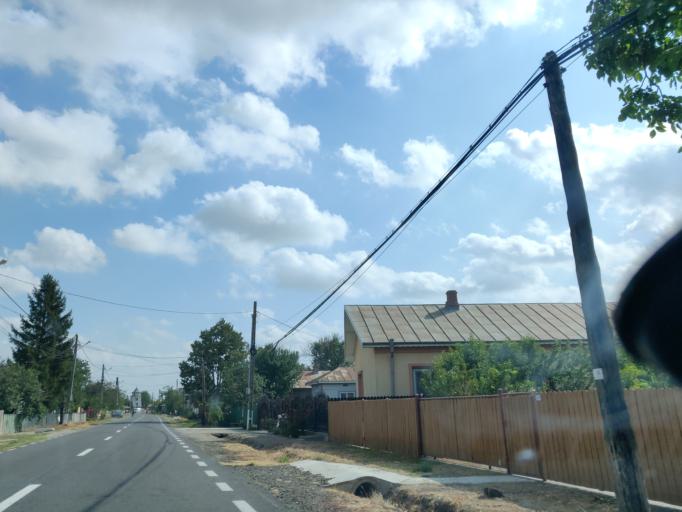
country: RO
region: Vrancea
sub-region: Comuna Ciorasti
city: Ciorasti
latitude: 45.4309
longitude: 27.3071
